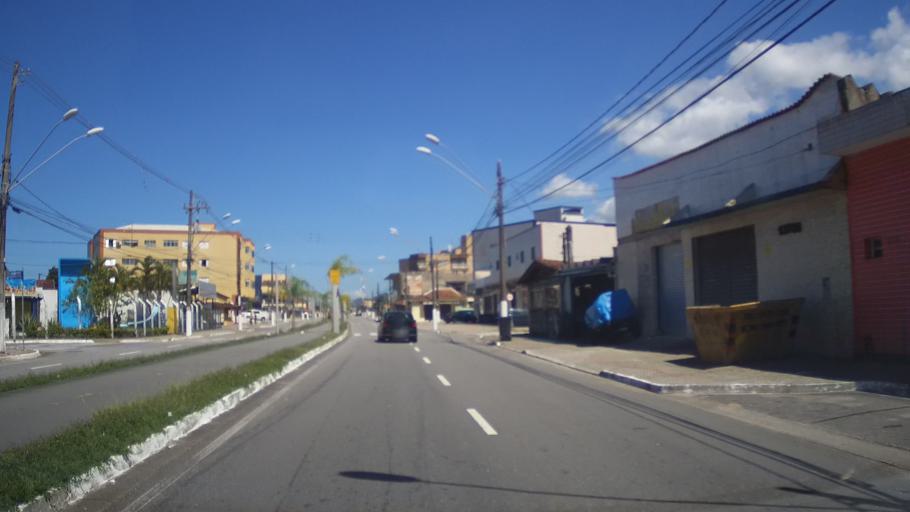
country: BR
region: Sao Paulo
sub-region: Mongagua
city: Mongagua
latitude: -24.0499
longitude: -46.5364
